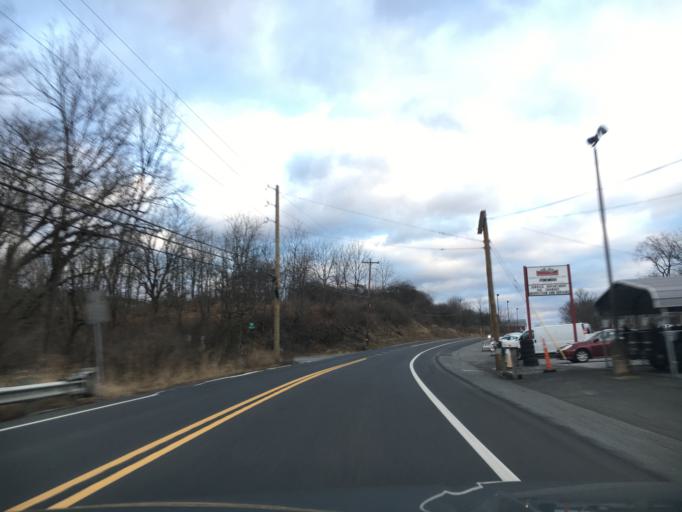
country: US
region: Pennsylvania
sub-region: Lehigh County
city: Schnecksville
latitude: 40.6858
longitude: -75.6795
